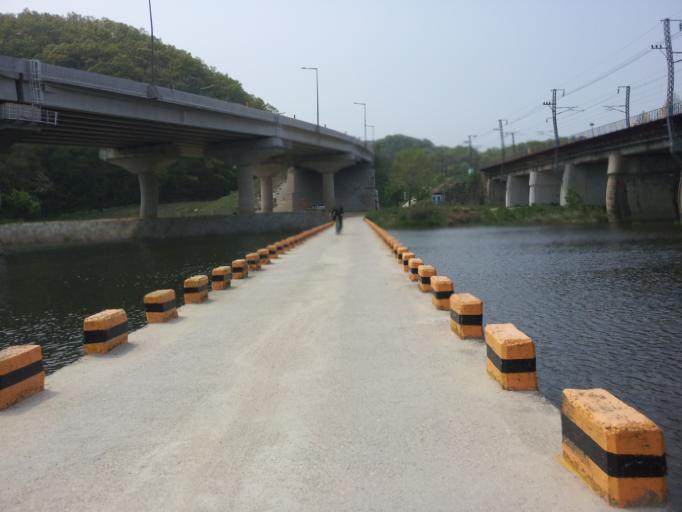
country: KR
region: Daejeon
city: Daejeon
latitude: 36.2755
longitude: 127.3461
